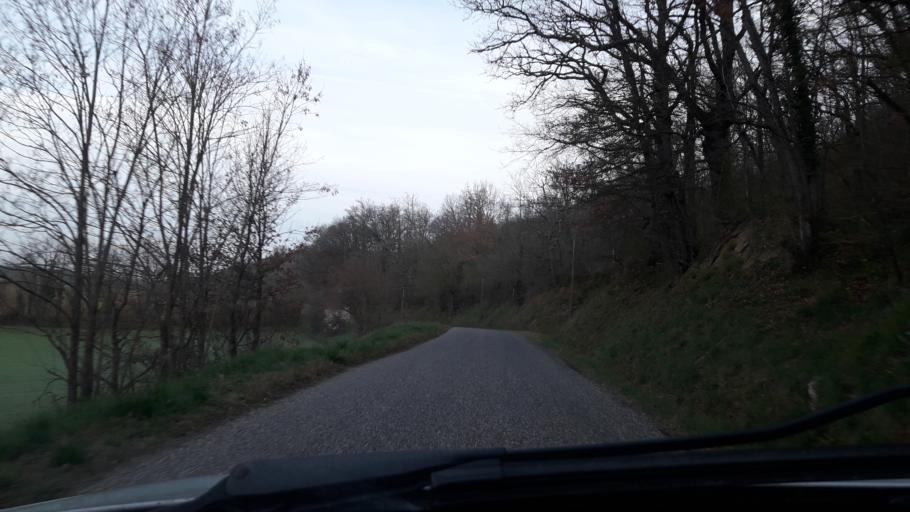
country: FR
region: Midi-Pyrenees
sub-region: Departement de la Haute-Garonne
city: Montesquieu-Volvestre
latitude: 43.1832
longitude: 1.2630
